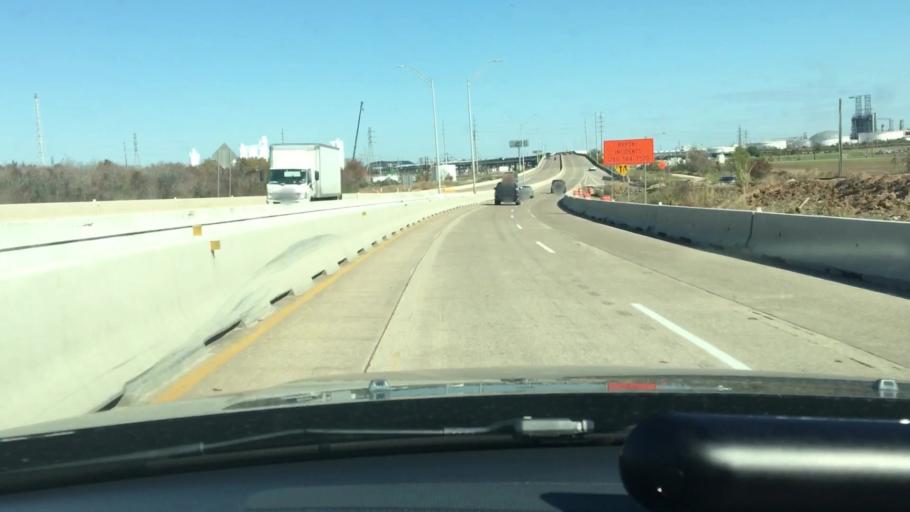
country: US
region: Texas
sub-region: Harris County
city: Deer Park
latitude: 29.7154
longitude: -95.1526
